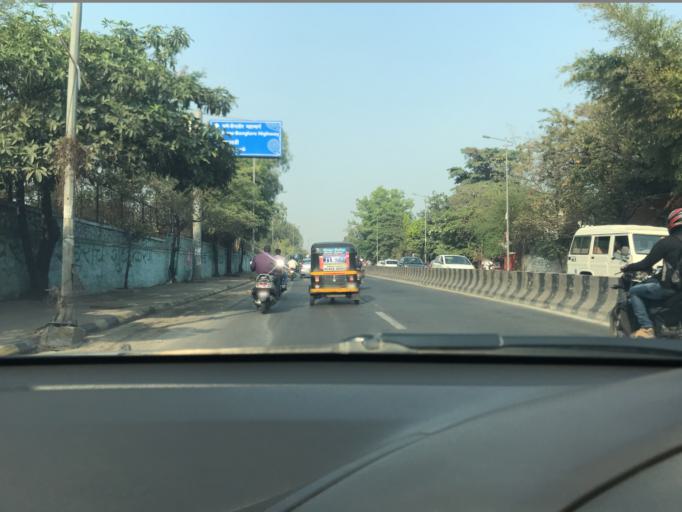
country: IN
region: Maharashtra
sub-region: Pune Division
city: Khadki
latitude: 18.5488
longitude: 73.8128
